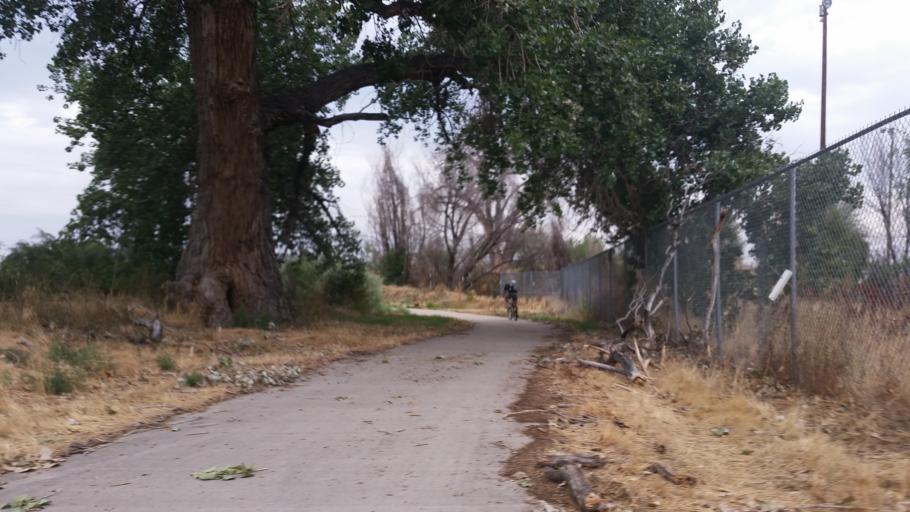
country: US
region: Colorado
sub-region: Adams County
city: Twin Lakes
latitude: 39.8144
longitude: -105.0140
